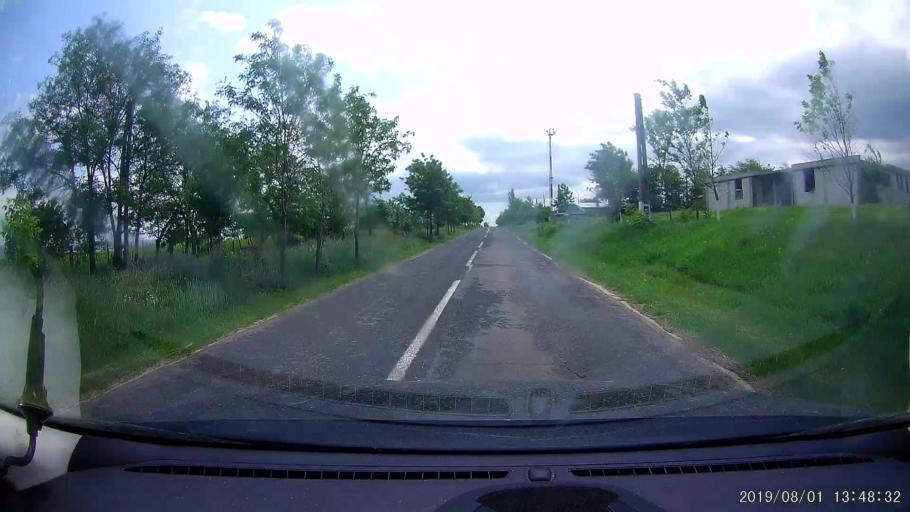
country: RO
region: Galati
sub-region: Comuna Oancea
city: Oancea
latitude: 45.9068
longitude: 28.1117
